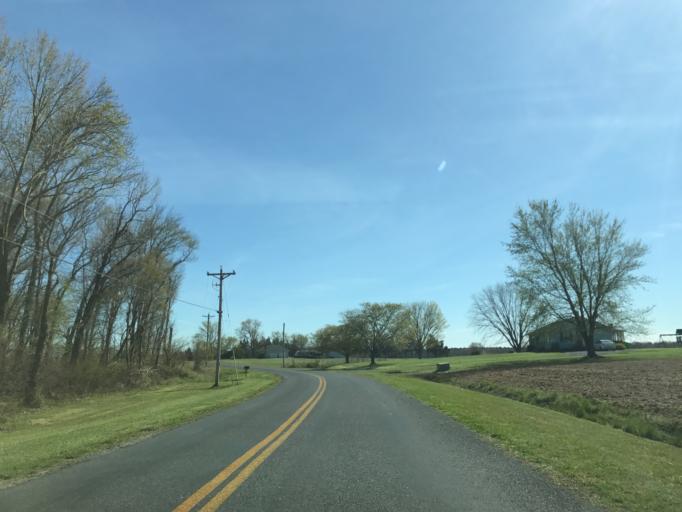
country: US
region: Maryland
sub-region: Queen Anne's County
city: Centreville
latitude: 39.0708
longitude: -75.9705
